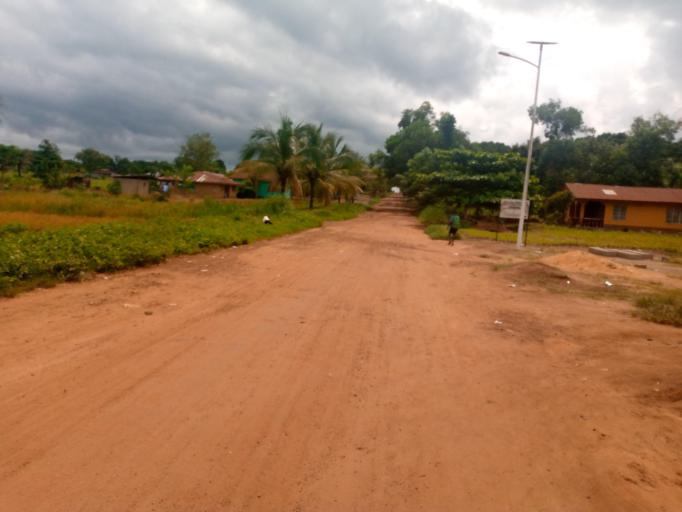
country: SL
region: Southern Province
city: Mogbwemo
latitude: 7.6116
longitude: -12.1796
